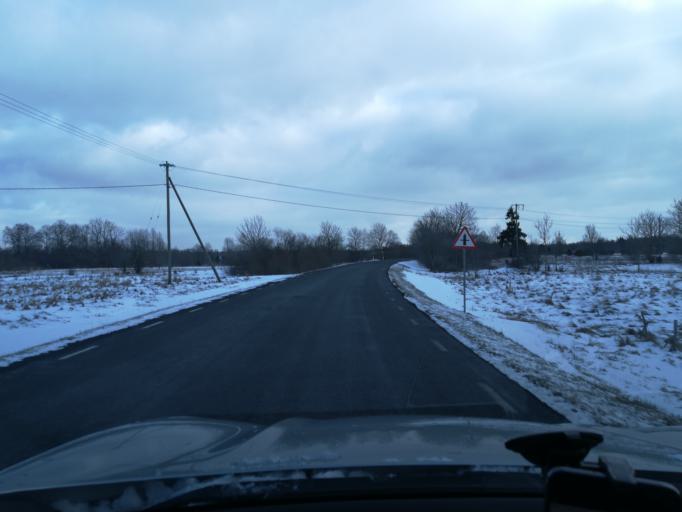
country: EE
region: Harju
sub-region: Harku vald
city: Tabasalu
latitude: 59.4262
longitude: 24.4183
